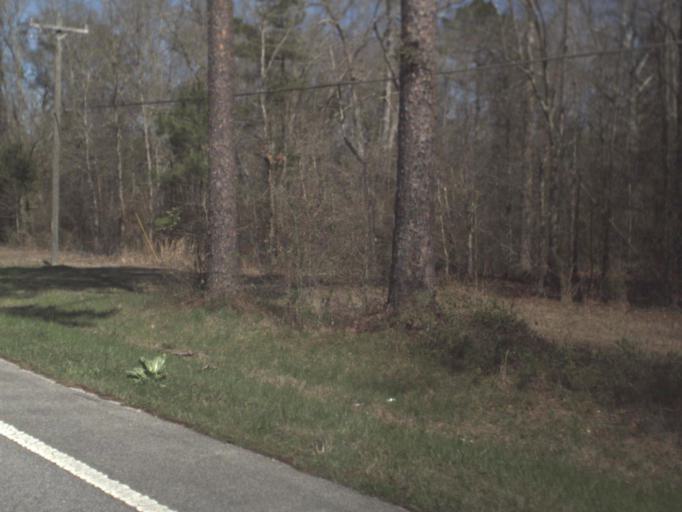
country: US
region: Florida
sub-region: Gadsden County
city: Gretna
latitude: 30.6847
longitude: -84.6203
